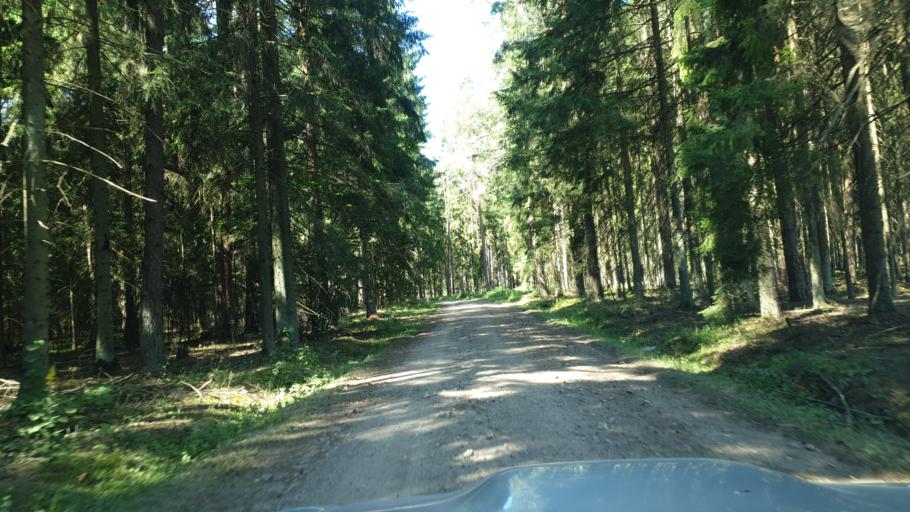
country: LT
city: Sirvintos
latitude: 54.9087
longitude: 24.9392
